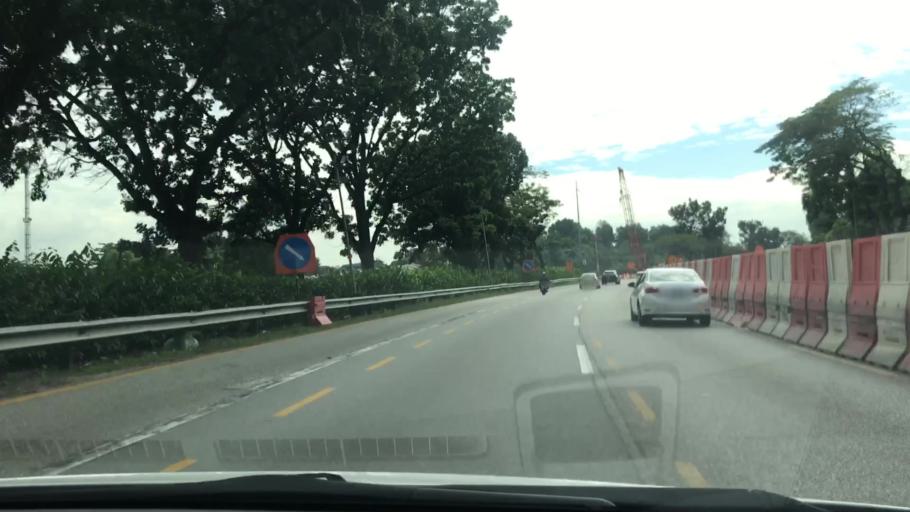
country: MY
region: Kuala Lumpur
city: Kuala Lumpur
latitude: 3.1123
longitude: 101.6860
